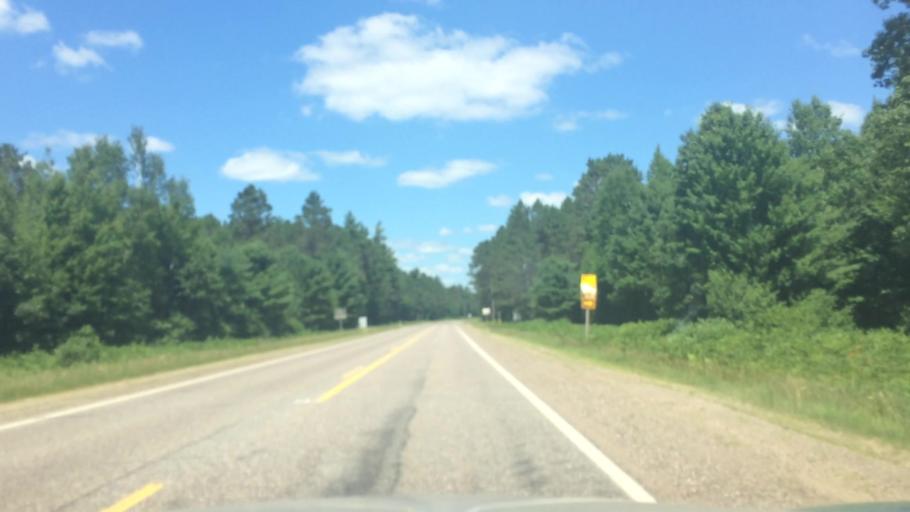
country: US
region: Wisconsin
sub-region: Vilas County
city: Lac du Flambeau
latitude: 46.0820
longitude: -89.6449
